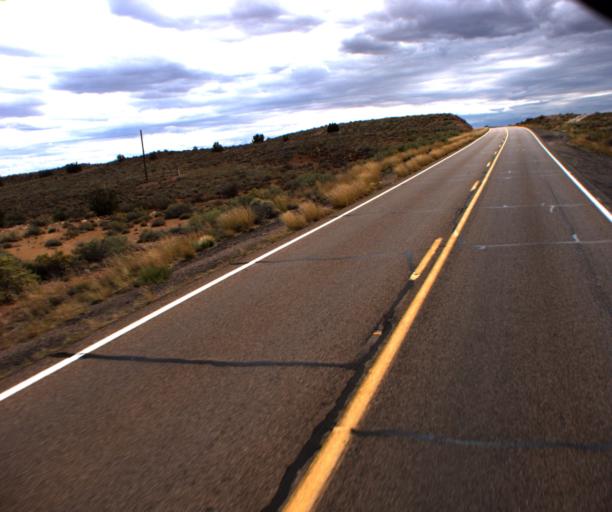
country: US
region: Arizona
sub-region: Navajo County
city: Holbrook
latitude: 34.8472
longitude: -110.1475
